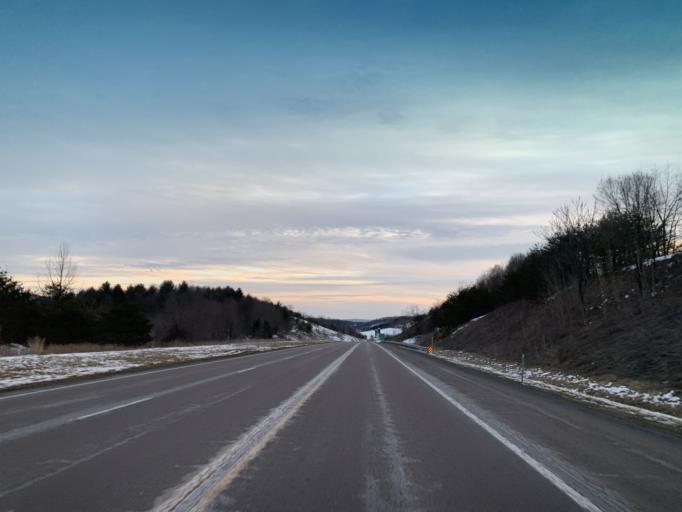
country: US
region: Maryland
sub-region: Allegany County
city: Cumberland
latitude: 39.7024
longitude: -78.7055
